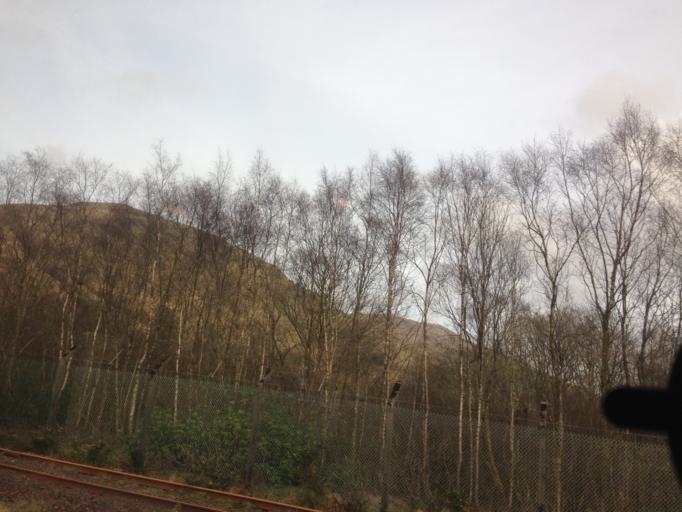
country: GB
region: Scotland
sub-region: Argyll and Bute
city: Garelochhead
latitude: 56.1574
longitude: -4.7793
